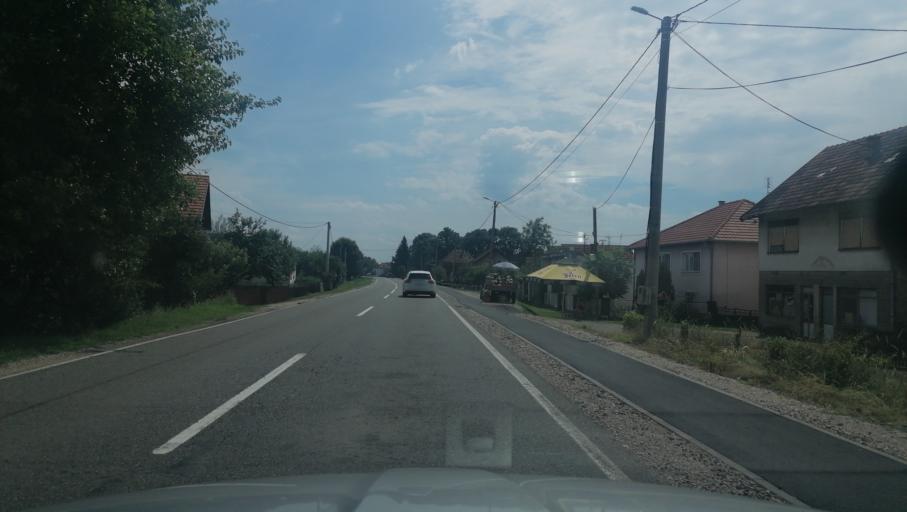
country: BA
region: Republika Srpska
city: Bosanski Samac
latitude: 45.0485
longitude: 18.4805
